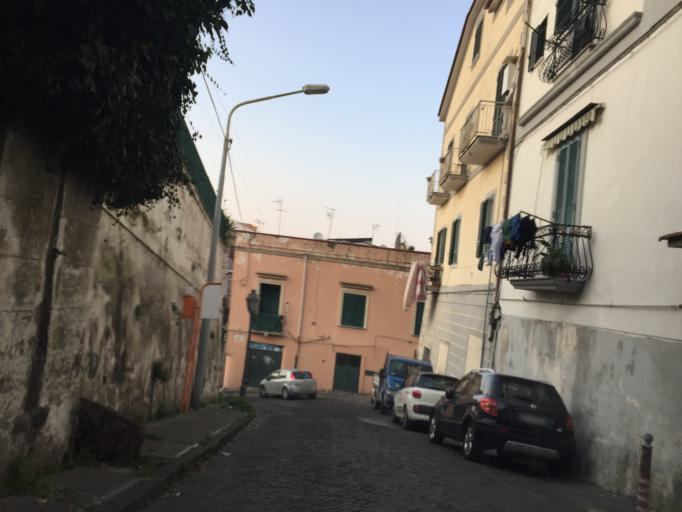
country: IT
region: Campania
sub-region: Provincia di Napoli
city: Castellammare di Stabia
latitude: 40.6888
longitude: 14.4819
